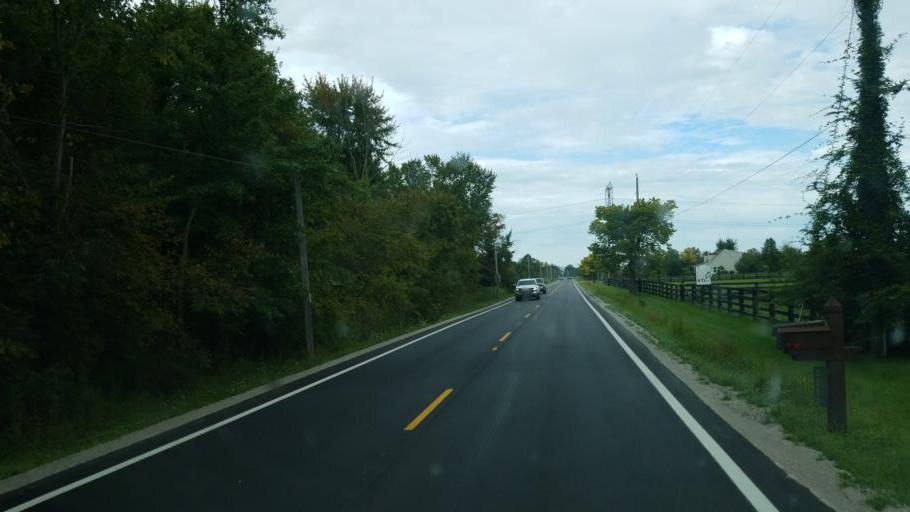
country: US
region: Ohio
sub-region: Franklin County
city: New Albany
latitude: 40.1211
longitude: -82.8106
